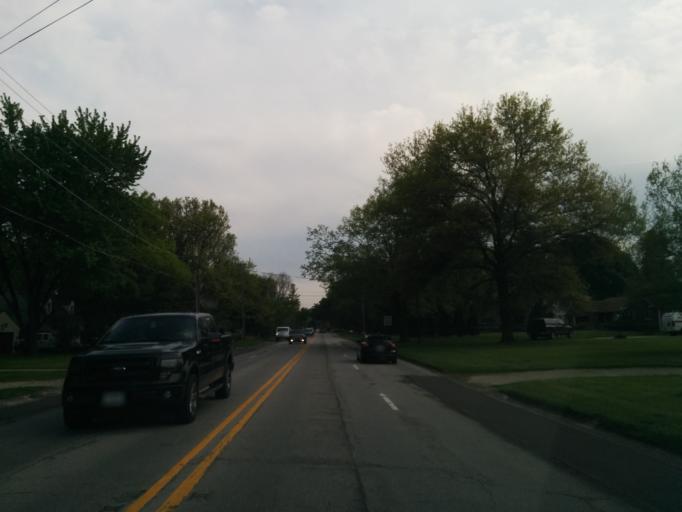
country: US
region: Illinois
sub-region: Kane County
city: North Aurora
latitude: 41.8157
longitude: -88.3278
